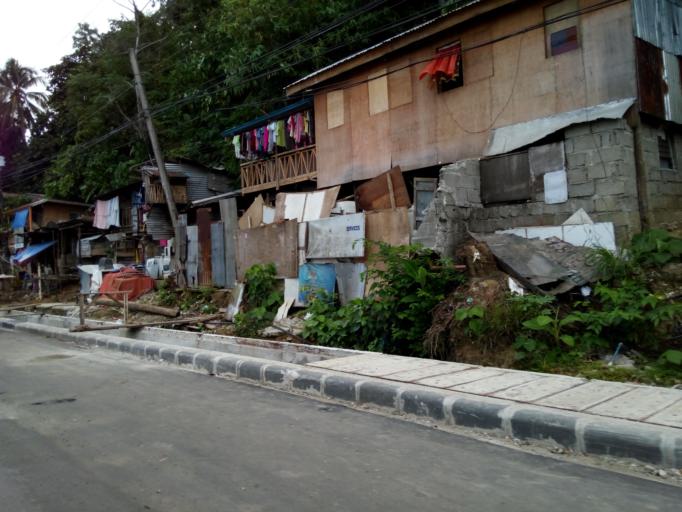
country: PH
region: Caraga
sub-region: Province of Surigao del Norte
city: Surigao
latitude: 9.7835
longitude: 125.4876
